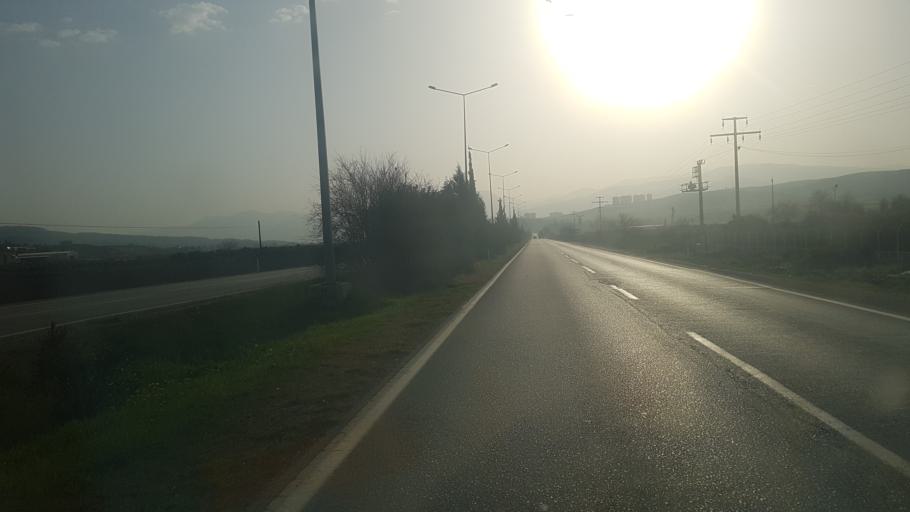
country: TR
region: Osmaniye
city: Toprakkale
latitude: 37.0548
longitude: 36.1334
